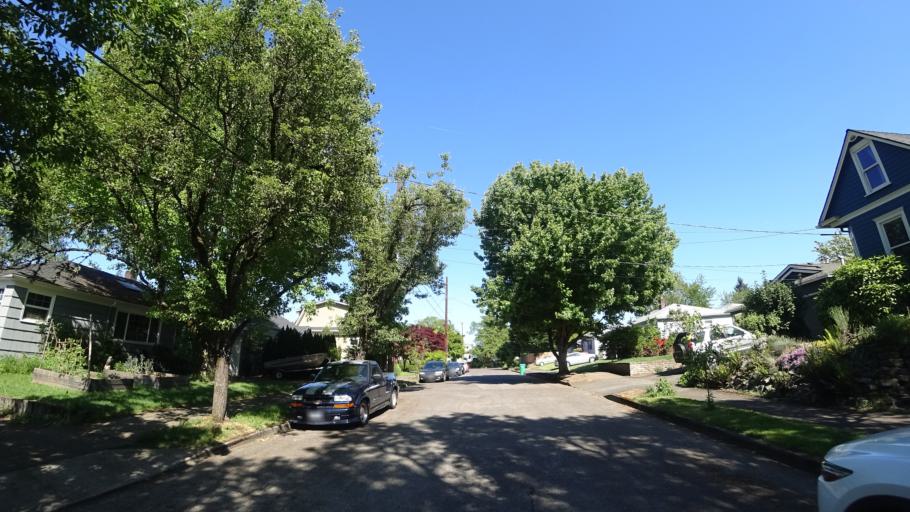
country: US
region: Oregon
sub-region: Clackamas County
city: Milwaukie
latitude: 45.4888
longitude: -122.6191
